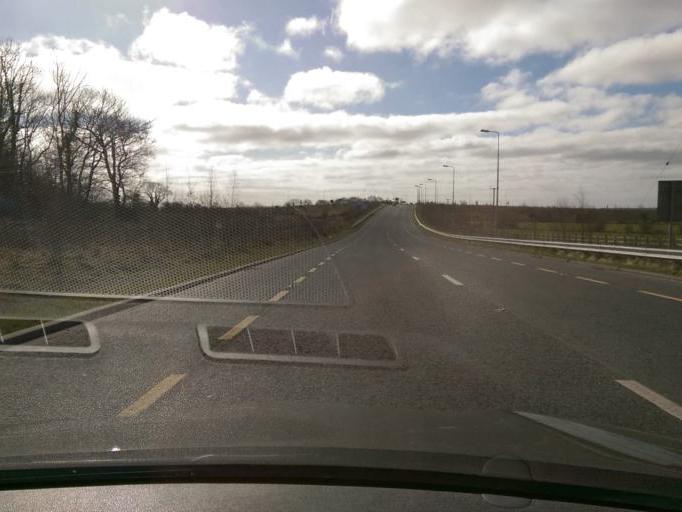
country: IE
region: Connaught
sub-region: County Galway
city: Ballinasloe
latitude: 53.3177
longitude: -8.1799
